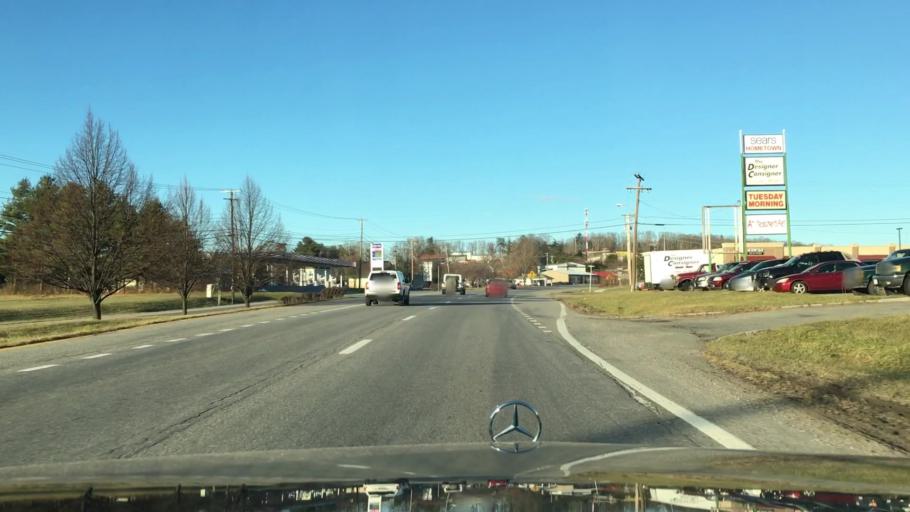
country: US
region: Virginia
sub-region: Montgomery County
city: Merrimac
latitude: 37.1728
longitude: -80.4202
